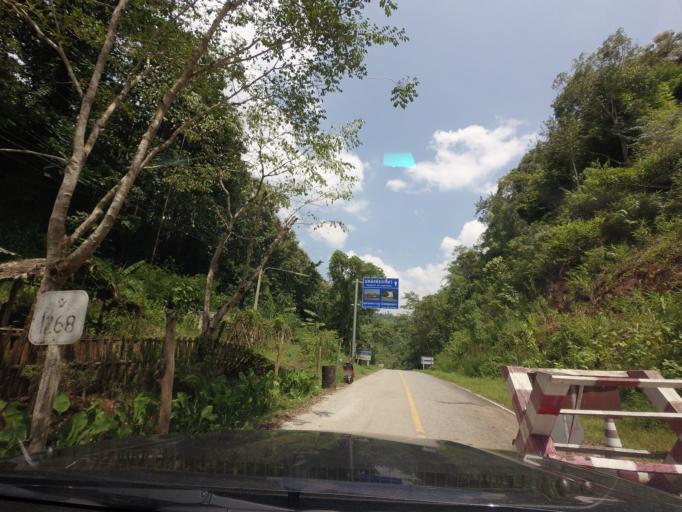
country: TH
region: Loei
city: Na Haeo
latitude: 17.6404
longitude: 100.9071
